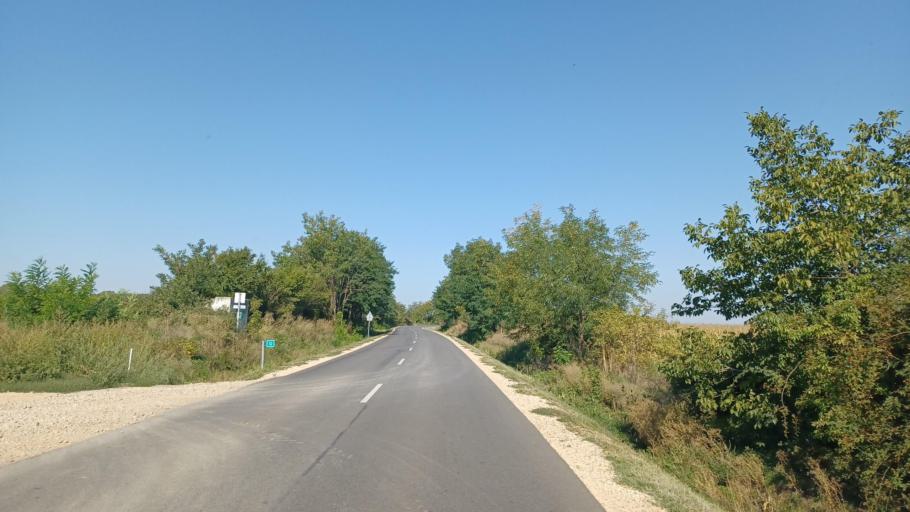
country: HU
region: Tolna
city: Nemetker
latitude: 46.6973
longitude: 18.7924
